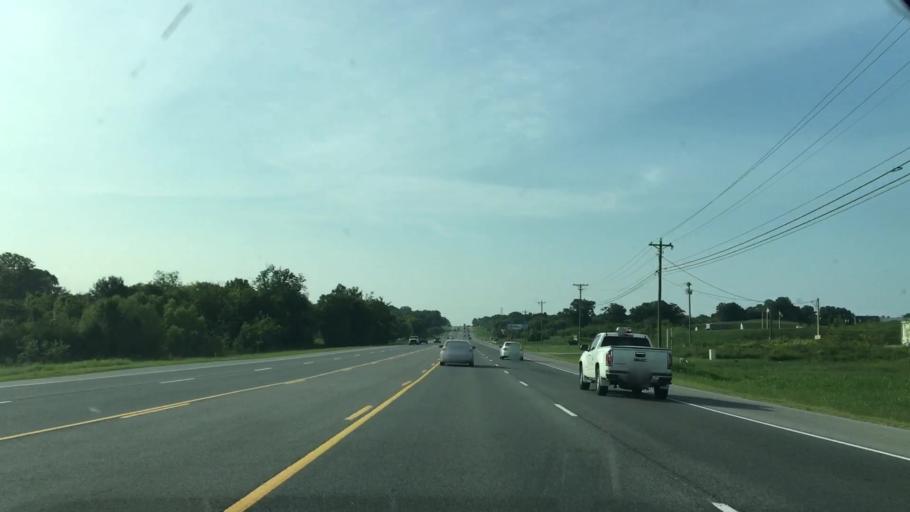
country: US
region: Tennessee
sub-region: Wilson County
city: Mount Juliet
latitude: 36.2226
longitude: -86.4252
